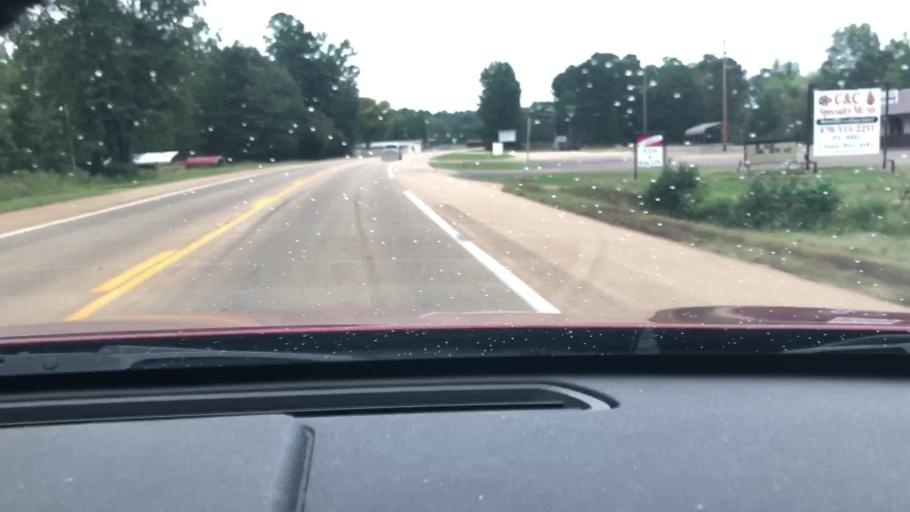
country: US
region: Arkansas
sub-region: Lafayette County
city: Stamps
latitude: 33.3674
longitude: -93.5169
